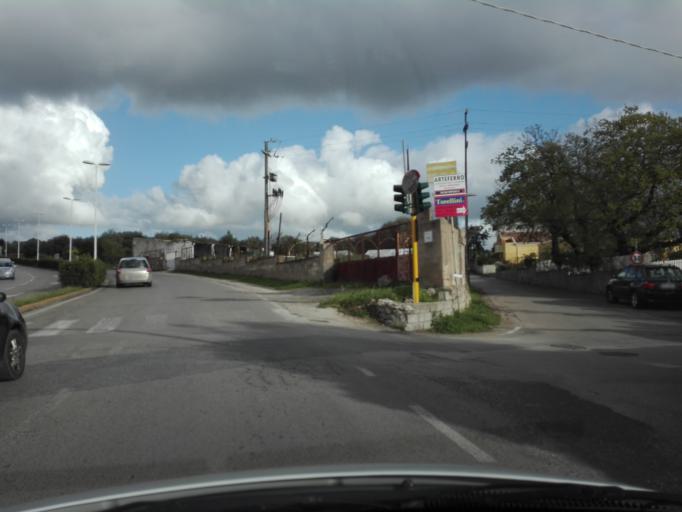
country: IT
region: Sardinia
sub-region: Provincia di Sassari
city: Sassari
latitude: 40.7108
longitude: 8.5721
